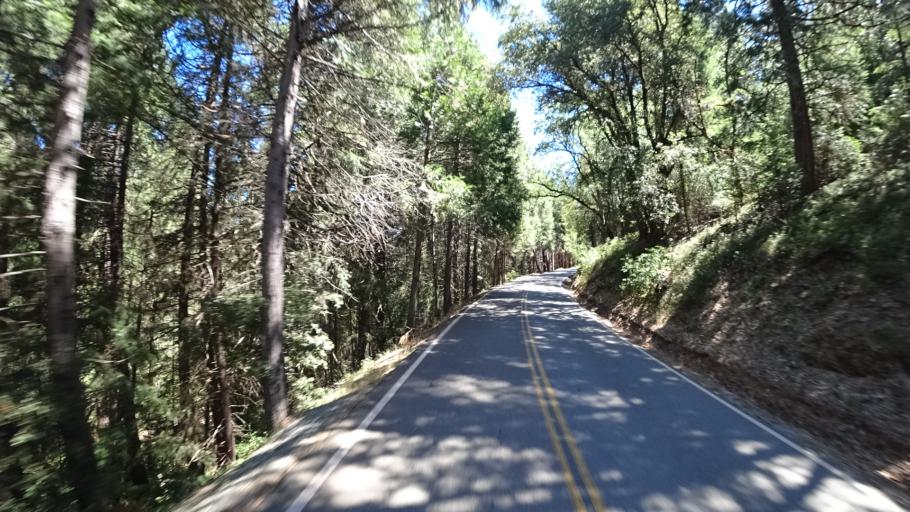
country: US
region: California
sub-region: Amador County
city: Pioneer
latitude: 38.3528
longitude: -120.5422
